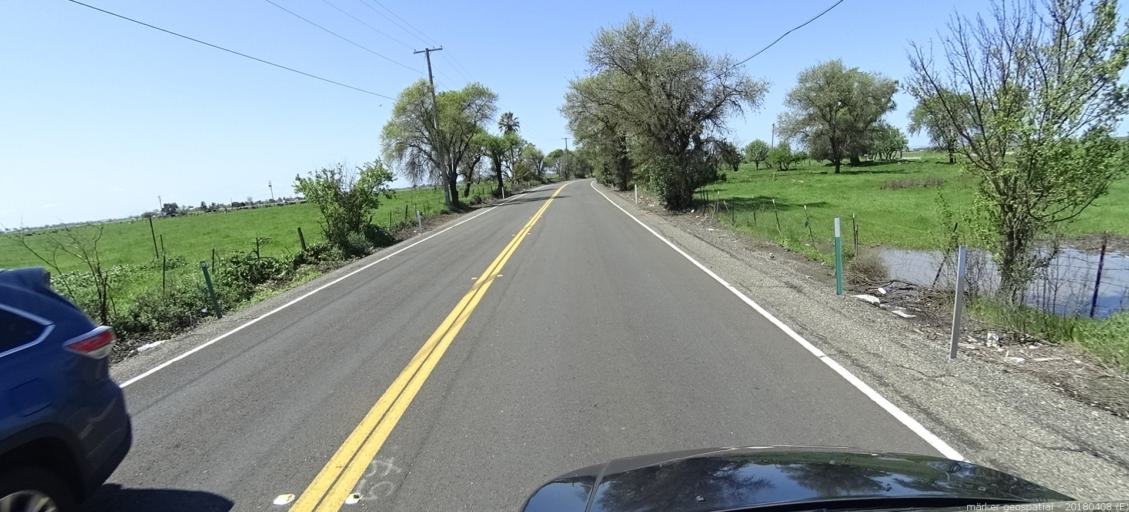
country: US
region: California
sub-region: Sacramento County
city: Laguna
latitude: 38.3758
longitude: -121.4697
